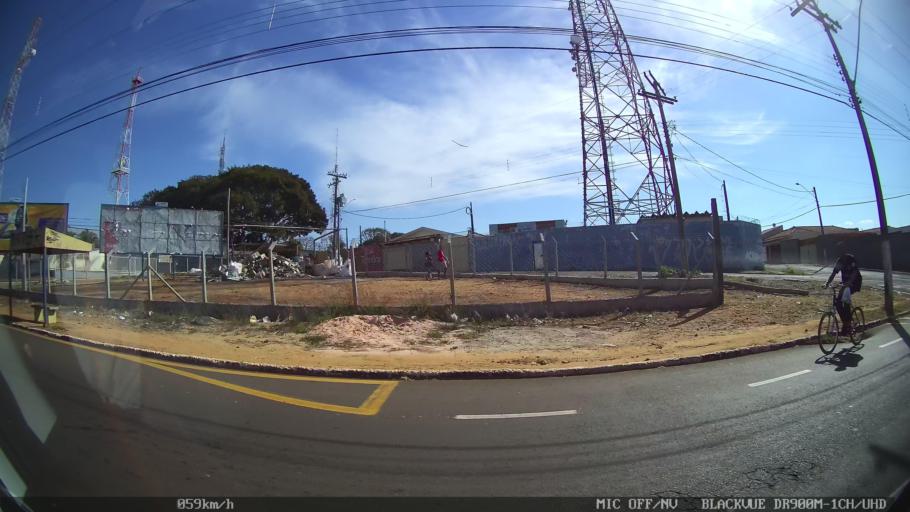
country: BR
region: Sao Paulo
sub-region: Franca
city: Franca
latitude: -20.5046
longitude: -47.3993
